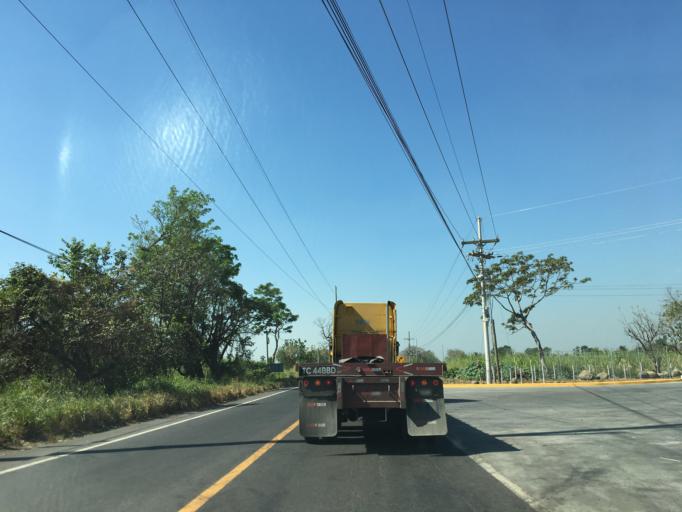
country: GT
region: Escuintla
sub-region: Municipio de Masagua
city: Masagua
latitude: 14.2482
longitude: -90.8077
